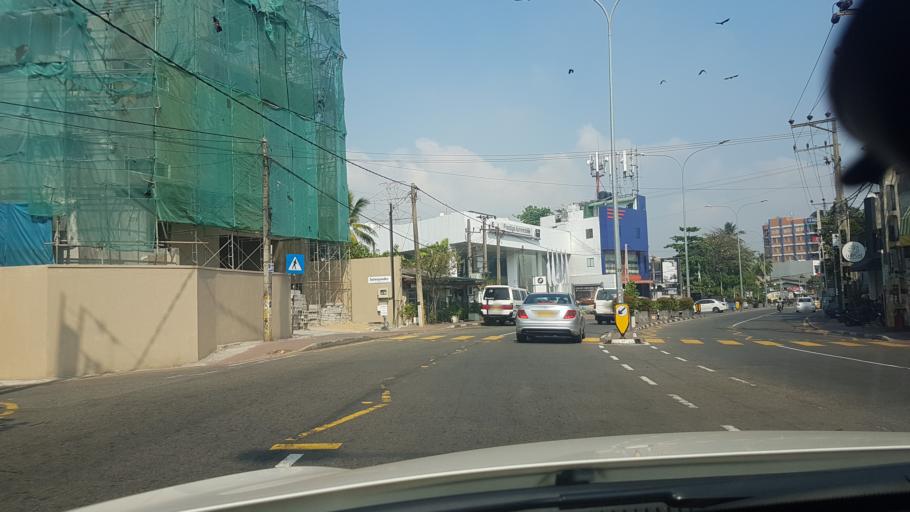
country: LK
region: Western
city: Battaramulla South
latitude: 6.8956
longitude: 79.9233
